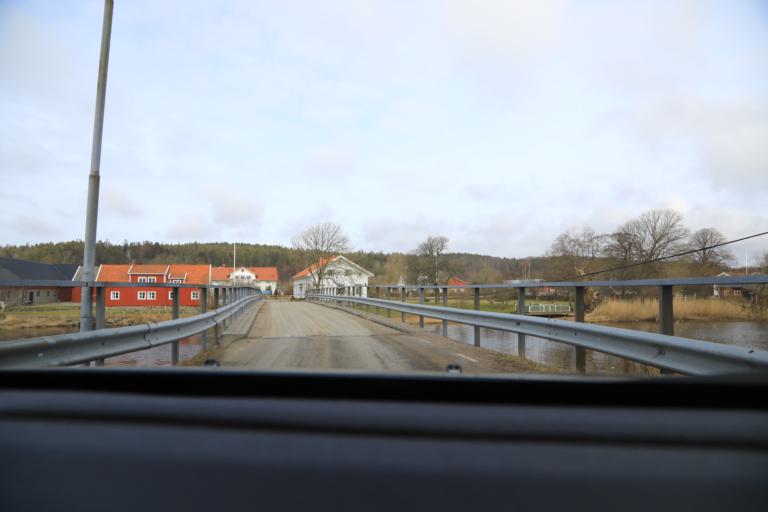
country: SE
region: Halland
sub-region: Varbergs Kommun
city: Veddige
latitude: 57.2296
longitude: 12.2320
